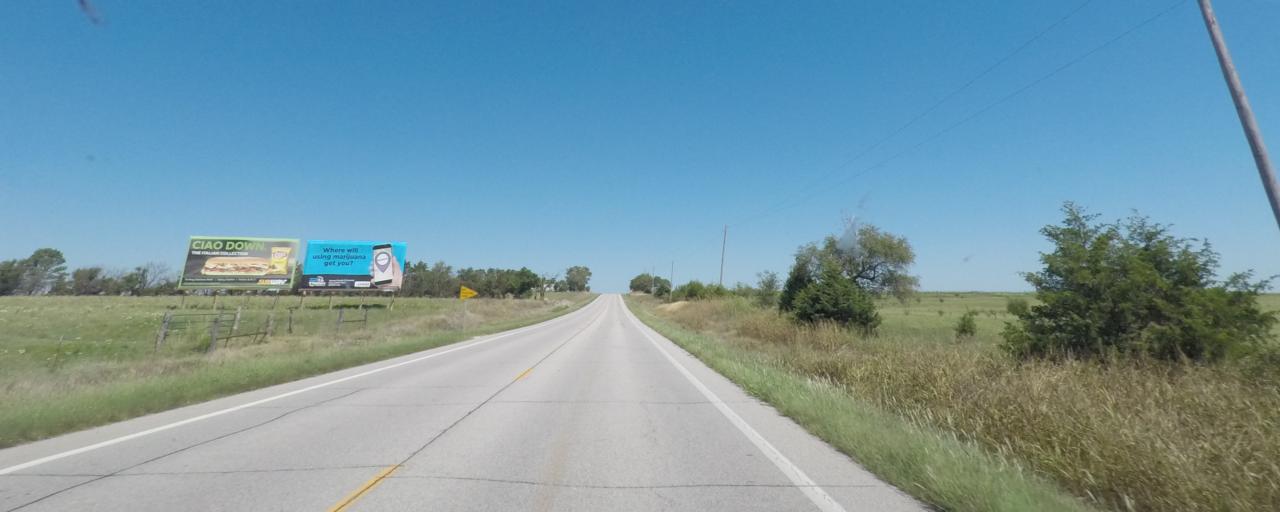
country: US
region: Kansas
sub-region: Sumner County
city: Wellington
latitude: 37.2273
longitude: -97.4025
